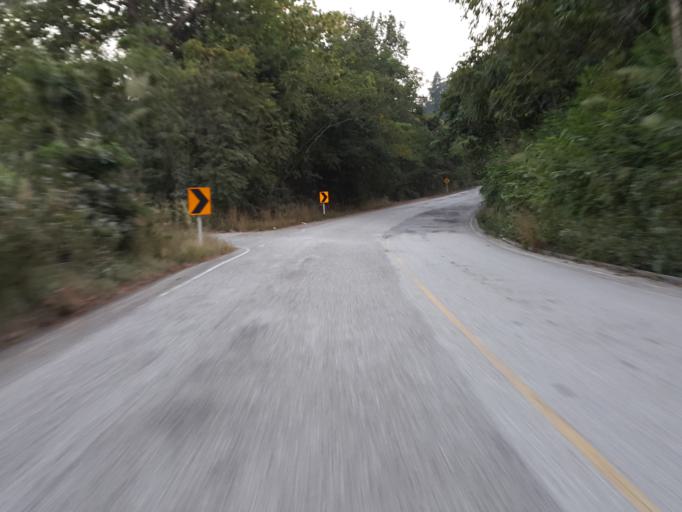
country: TH
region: Lampang
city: Thoen
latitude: 17.6732
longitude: 99.1117
